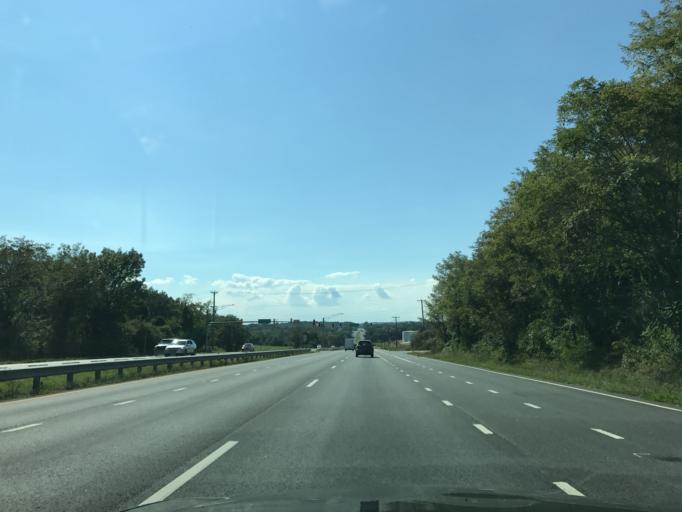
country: US
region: Maryland
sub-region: Cecil County
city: Charlestown
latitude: 39.5830
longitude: -76.0202
